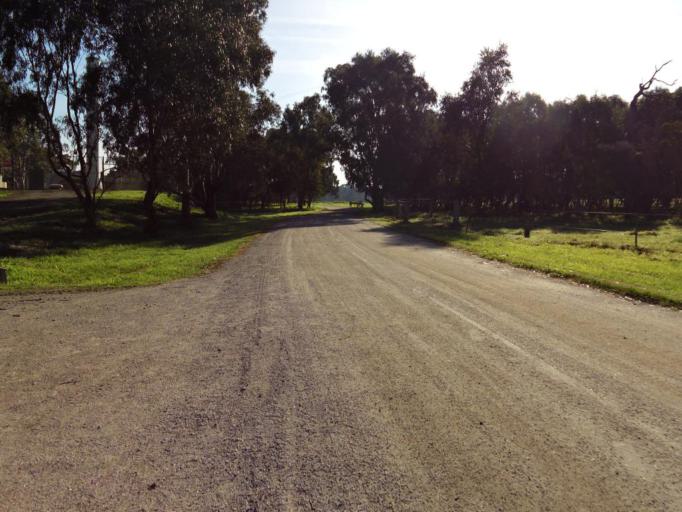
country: AU
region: Victoria
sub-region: Kingston
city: Waterways
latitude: -38.0017
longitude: 145.1264
